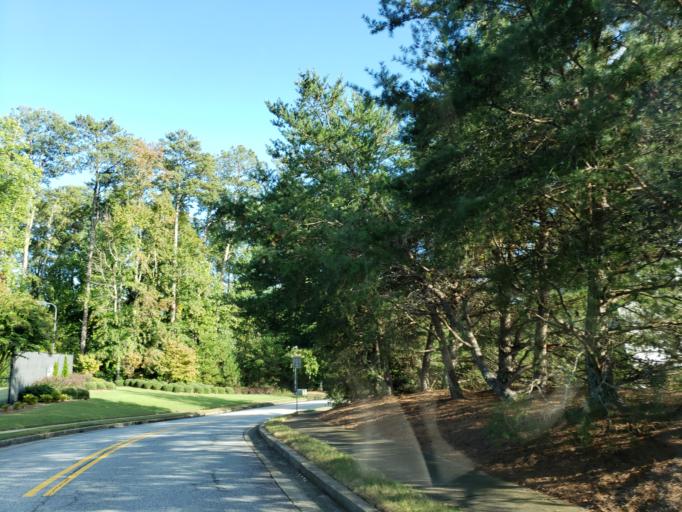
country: US
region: Georgia
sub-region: Cobb County
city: Marietta
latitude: 33.9885
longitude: -84.5042
